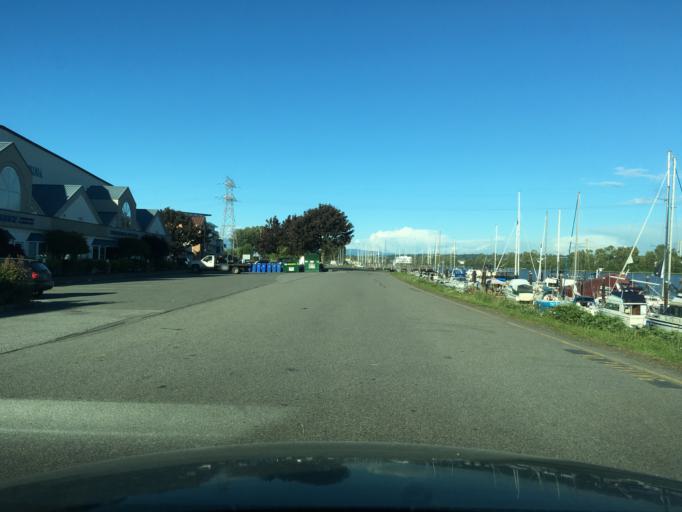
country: CA
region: British Columbia
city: Delta
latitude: 49.1631
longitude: -122.9910
